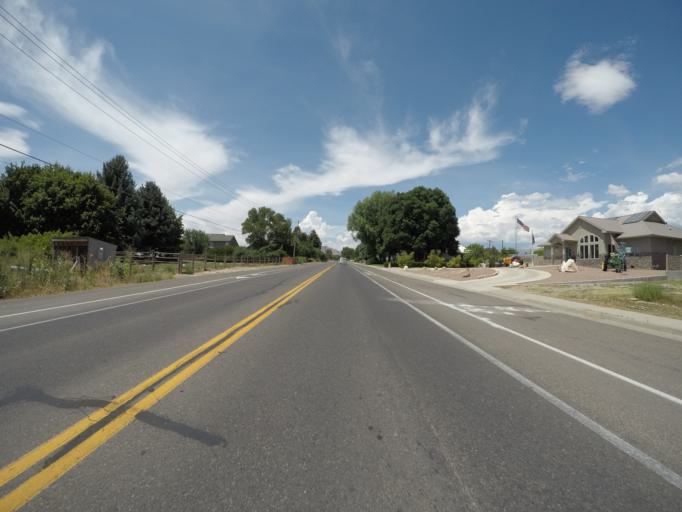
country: US
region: Utah
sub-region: Uintah County
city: Vernal
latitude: 40.4484
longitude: -109.5330
